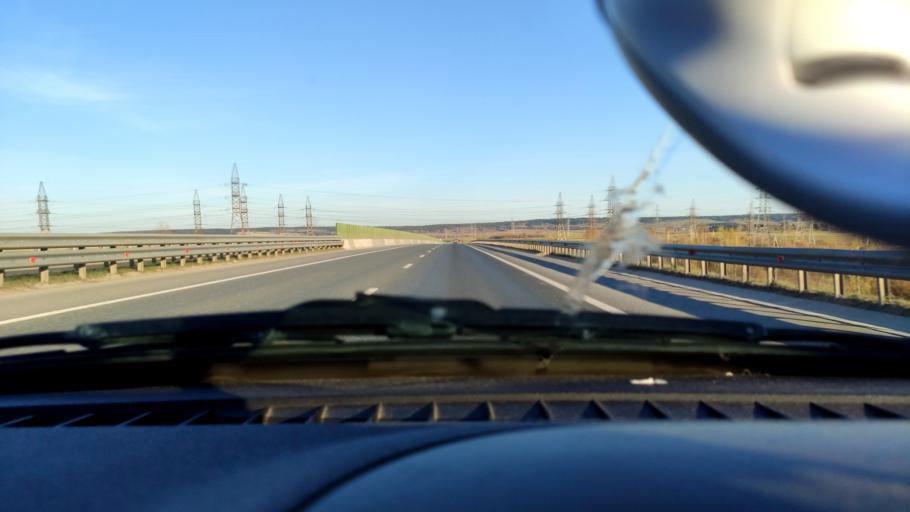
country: RU
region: Perm
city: Froly
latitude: 57.9312
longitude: 56.2981
